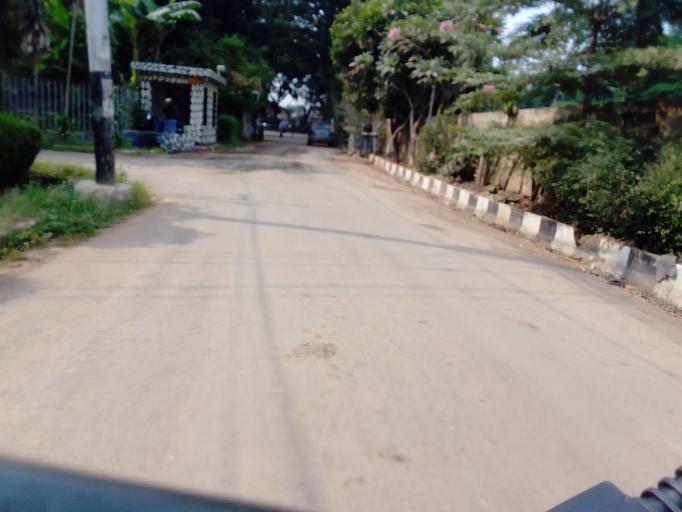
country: ID
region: Jakarta Raya
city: Jakarta
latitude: -6.2021
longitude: 106.8109
